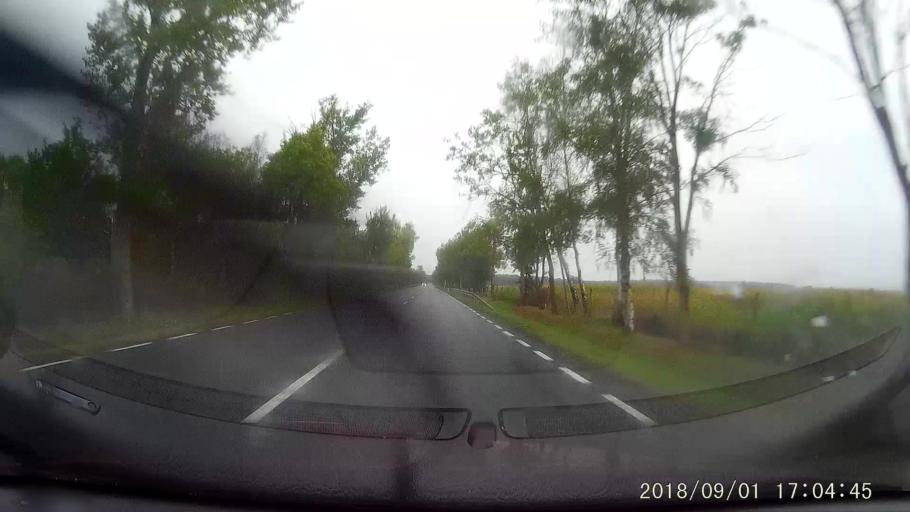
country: PL
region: Lubusz
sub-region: Powiat zielonogorski
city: Swidnica
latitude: 51.8616
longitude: 15.3589
